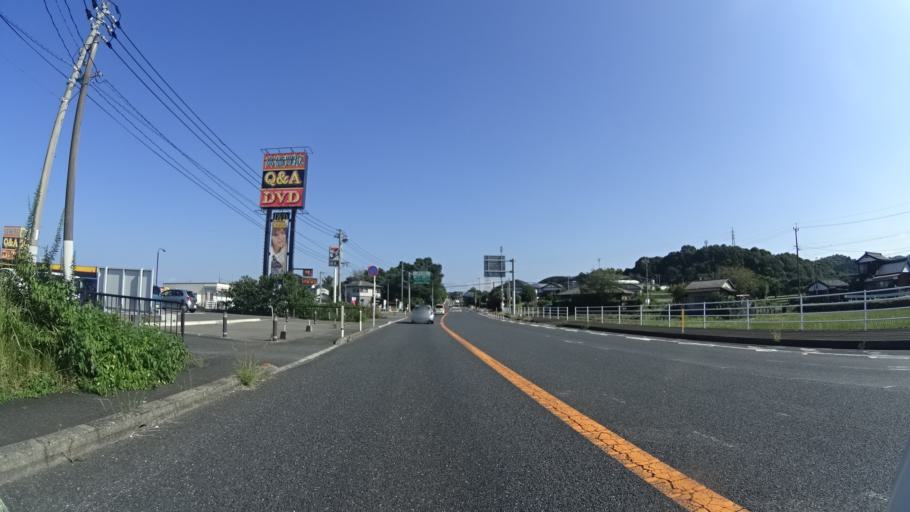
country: JP
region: Fukuoka
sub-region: Buzen-shi
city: Buzen
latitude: 33.6159
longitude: 131.0999
